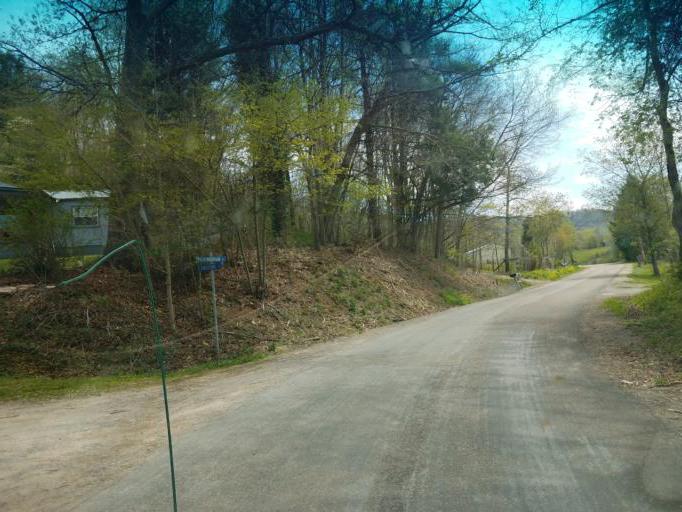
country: US
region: Virginia
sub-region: Smyth County
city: Marion
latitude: 36.8050
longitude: -81.4634
